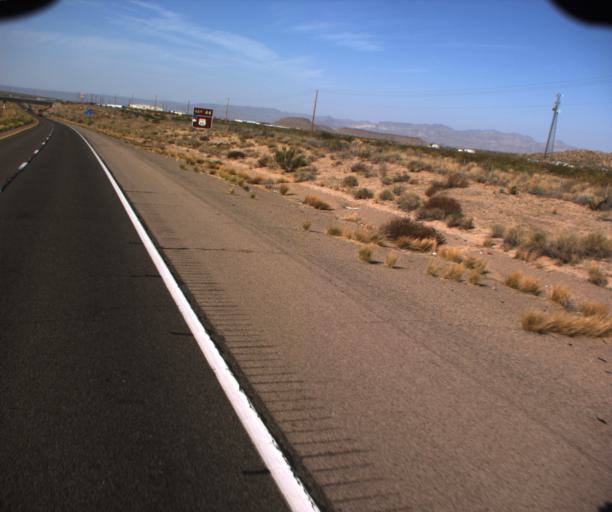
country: US
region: Arizona
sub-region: Mohave County
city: Kingman
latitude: 35.1510
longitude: -114.0919
